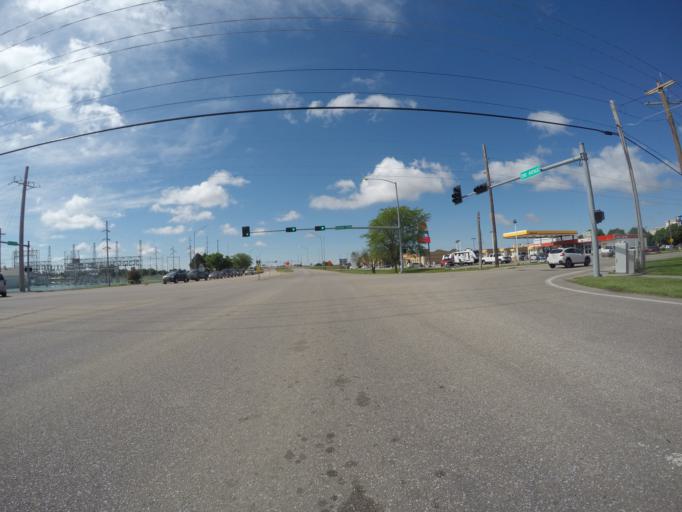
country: US
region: Nebraska
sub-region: Buffalo County
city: Kearney
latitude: 40.6736
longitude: -99.0859
